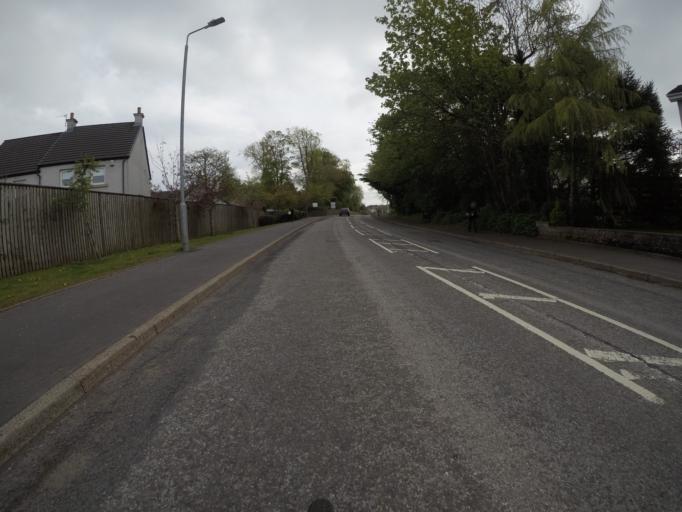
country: GB
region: Scotland
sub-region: East Renfrewshire
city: Busby
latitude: 55.7754
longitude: -4.3049
